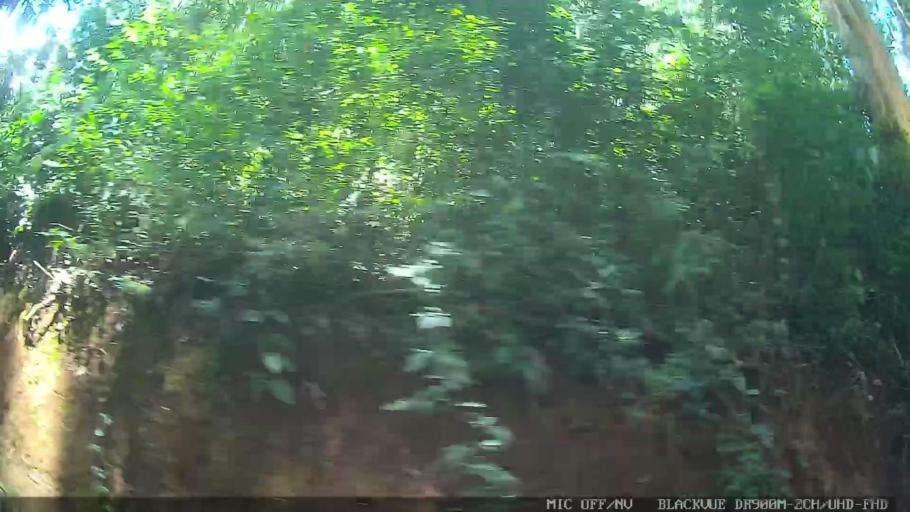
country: BR
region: Minas Gerais
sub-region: Extrema
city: Extrema
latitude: -22.8873
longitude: -46.2949
